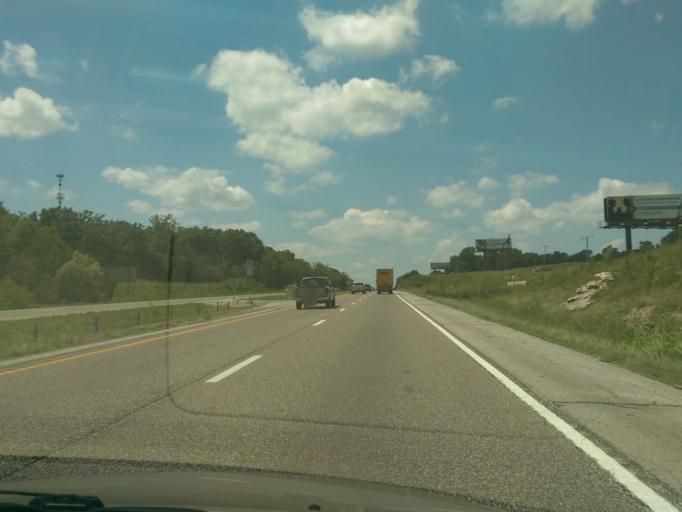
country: US
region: Missouri
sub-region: Boone County
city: Columbia
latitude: 38.9721
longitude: -92.4382
